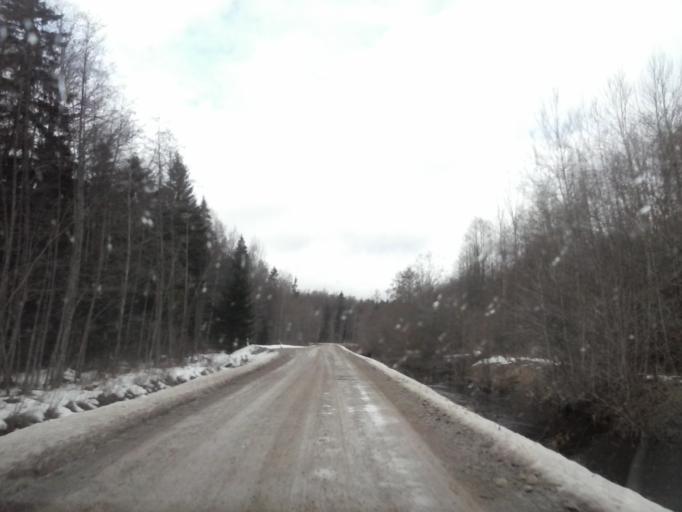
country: EE
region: Jogevamaa
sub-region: Mustvee linn
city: Mustvee
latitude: 59.0767
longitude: 26.8786
